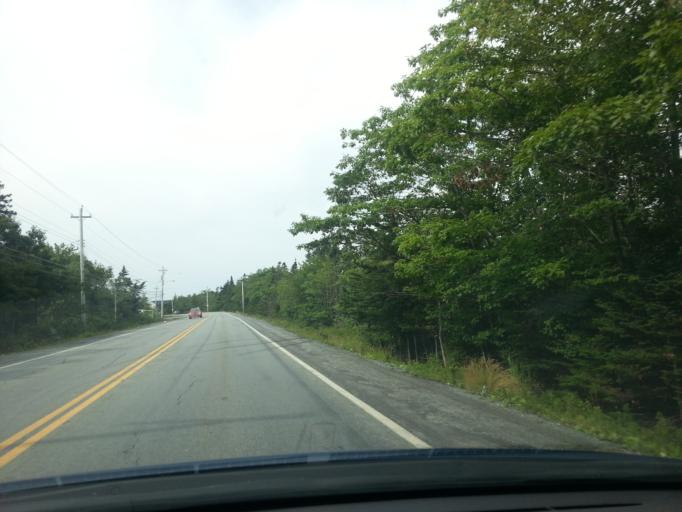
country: CA
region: Nova Scotia
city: Halifax
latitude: 44.5779
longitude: -63.7094
